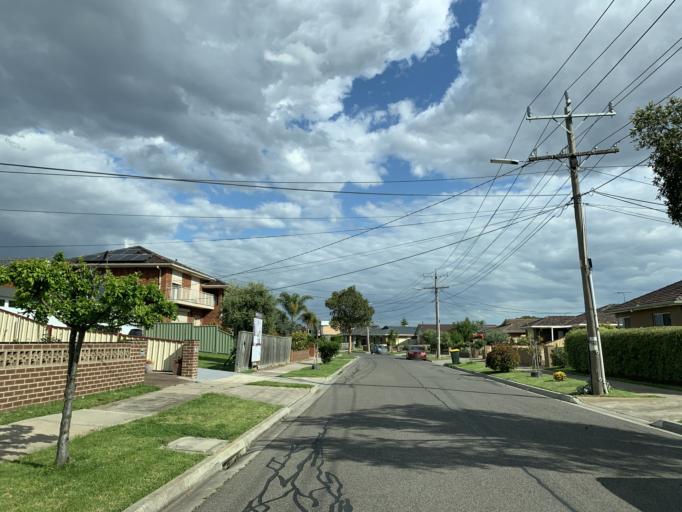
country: AU
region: Victoria
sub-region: Moonee Valley
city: Keilor East
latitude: -37.7450
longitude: 144.8508
